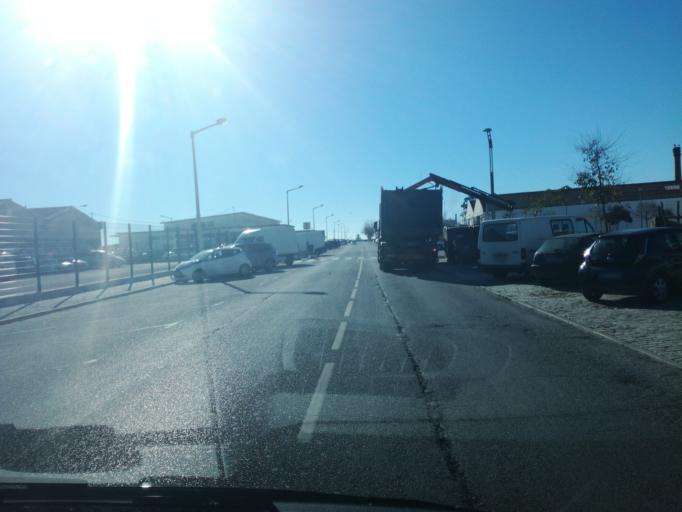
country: PT
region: Faro
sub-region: Olhao
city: Olhao
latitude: 37.0279
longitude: -7.8364
